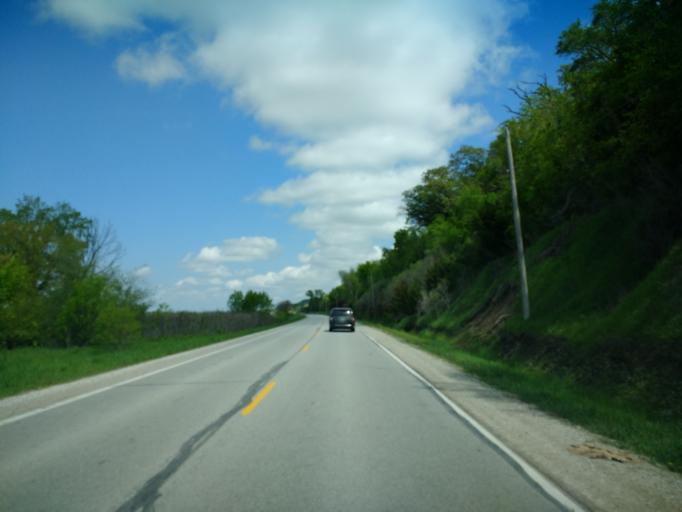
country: US
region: Iowa
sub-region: Harrison County
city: Missouri Valley
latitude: 41.4437
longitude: -95.8705
